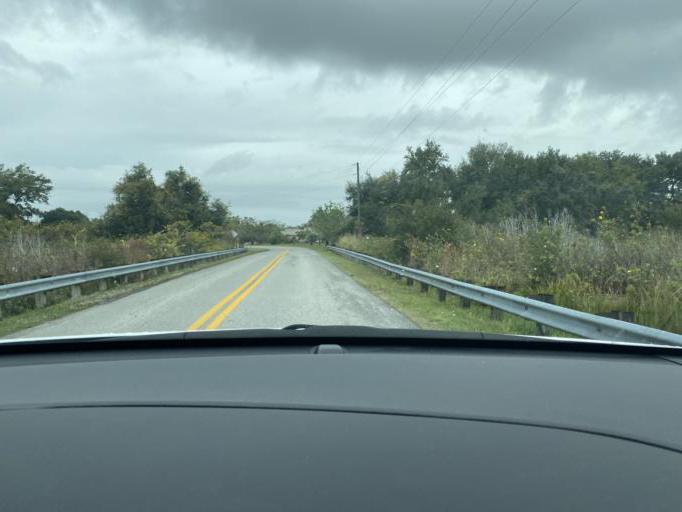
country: US
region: Florida
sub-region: Lake County
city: Minneola
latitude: 28.5954
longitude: -81.7876
